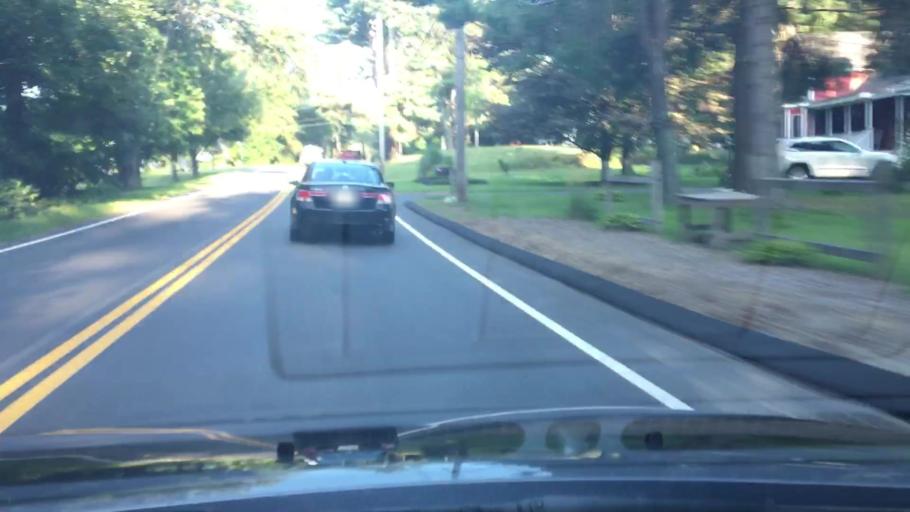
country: US
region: Massachusetts
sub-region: Middlesex County
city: Hopkinton
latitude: 42.2417
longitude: -71.5720
